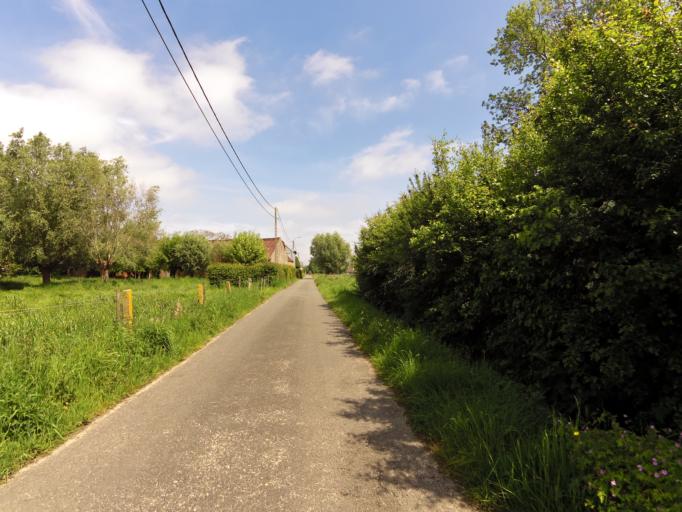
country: BE
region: Flanders
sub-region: Provincie West-Vlaanderen
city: Ichtegem
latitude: 51.1017
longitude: 3.0063
